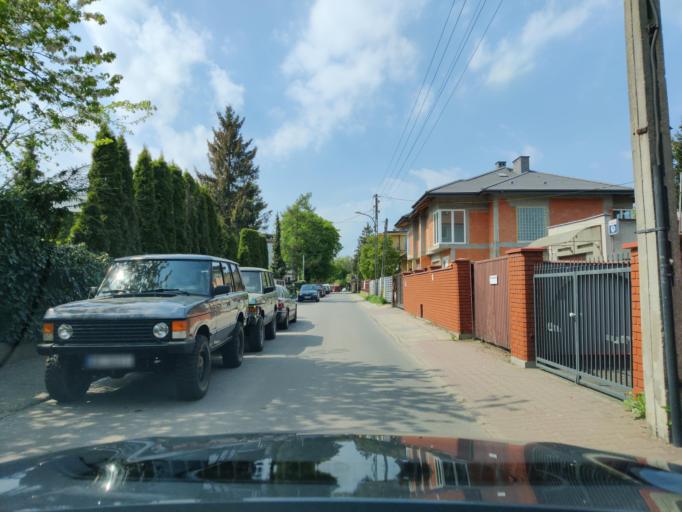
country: PL
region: Masovian Voivodeship
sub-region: Warszawa
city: Wlochy
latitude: 52.1857
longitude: 20.9593
